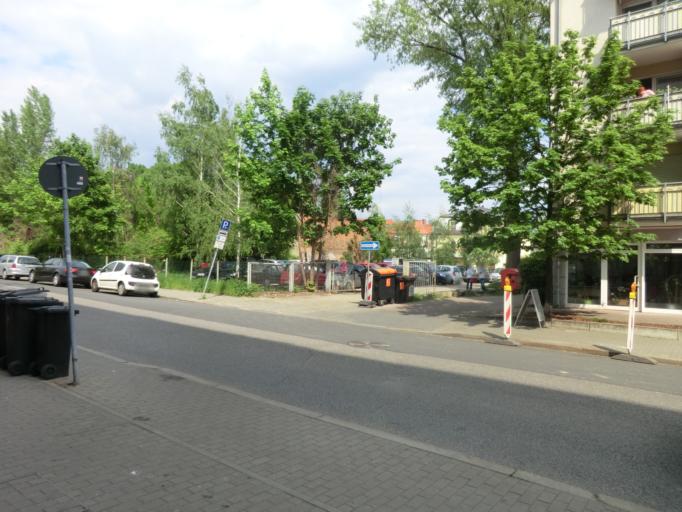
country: DE
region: Saxony
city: Dresden
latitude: 51.0443
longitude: 13.7022
